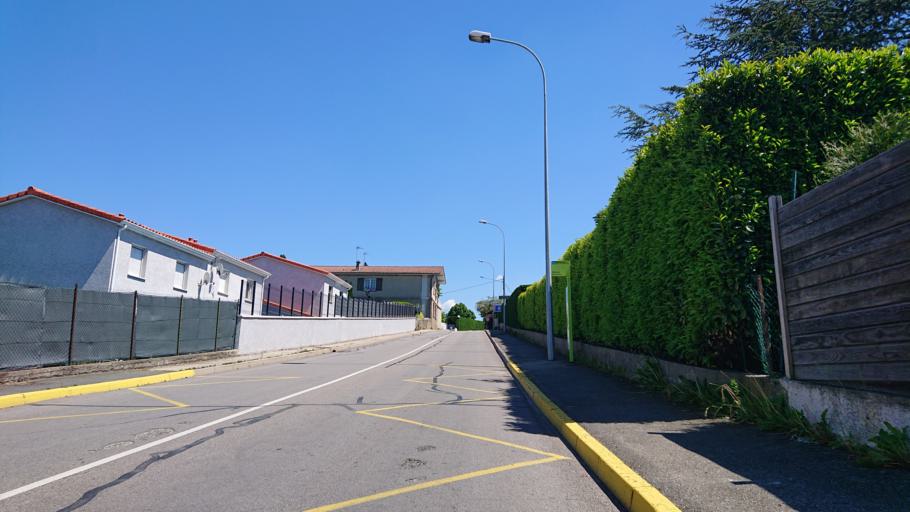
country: FR
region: Rhone-Alpes
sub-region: Departement de la Loire
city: Villars
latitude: 45.4538
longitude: 4.3573
